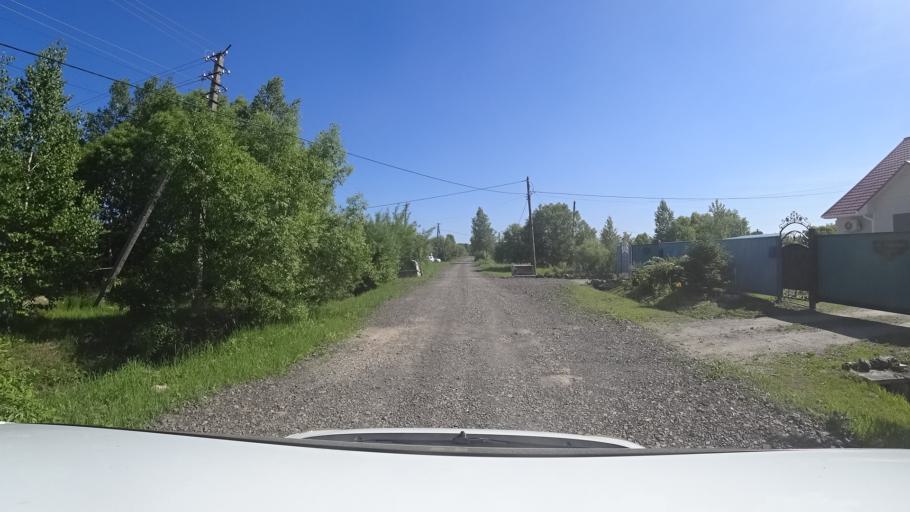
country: RU
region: Khabarovsk Krai
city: Topolevo
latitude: 48.5530
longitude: 135.1690
